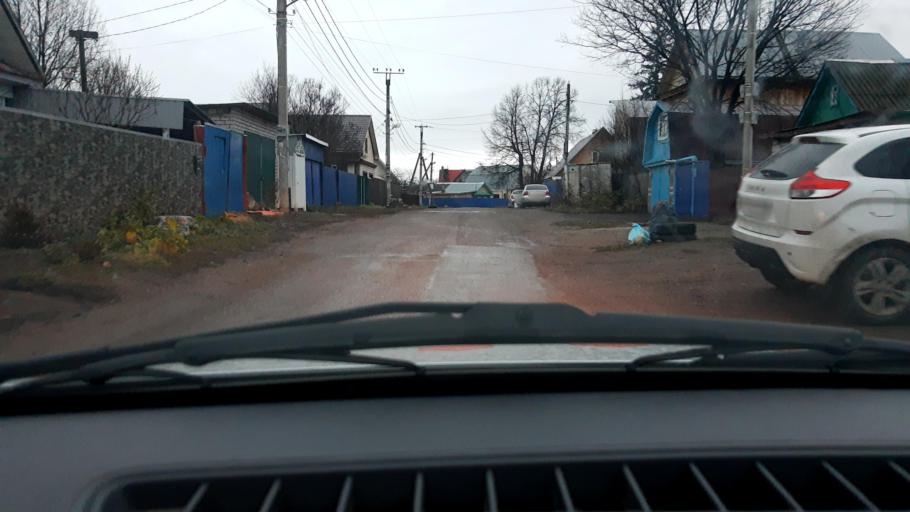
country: RU
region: Bashkortostan
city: Mikhaylovka
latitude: 54.7947
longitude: 55.8829
